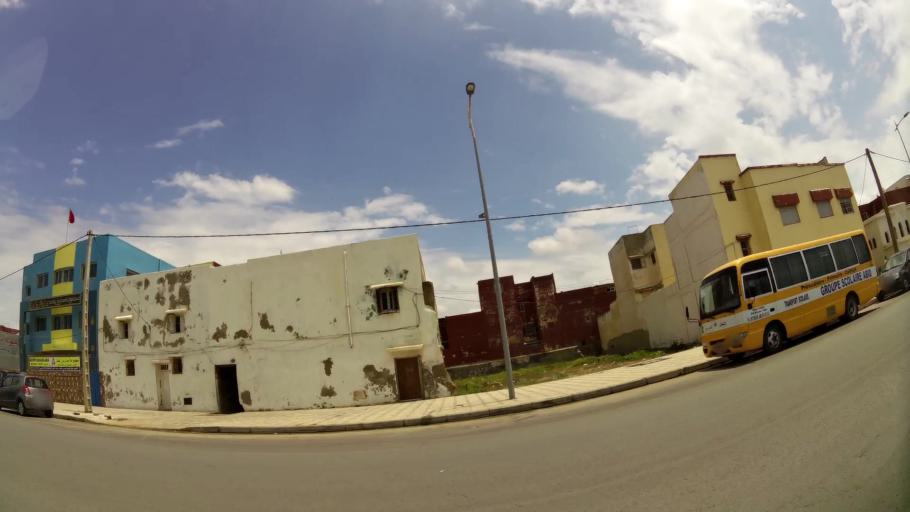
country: MA
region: Rabat-Sale-Zemmour-Zaer
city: Sale
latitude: 34.0484
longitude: -6.8275
